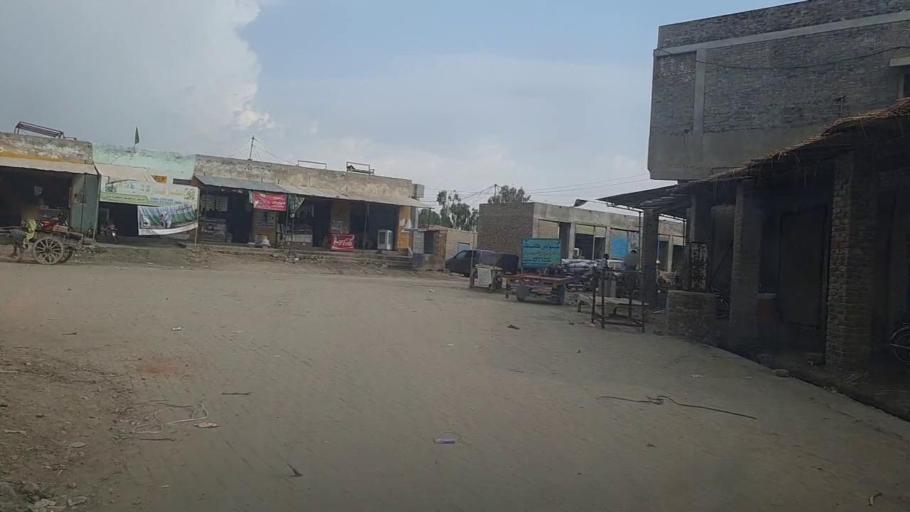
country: PK
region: Sindh
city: Mirpur Mathelo
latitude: 27.9171
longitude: 69.5217
